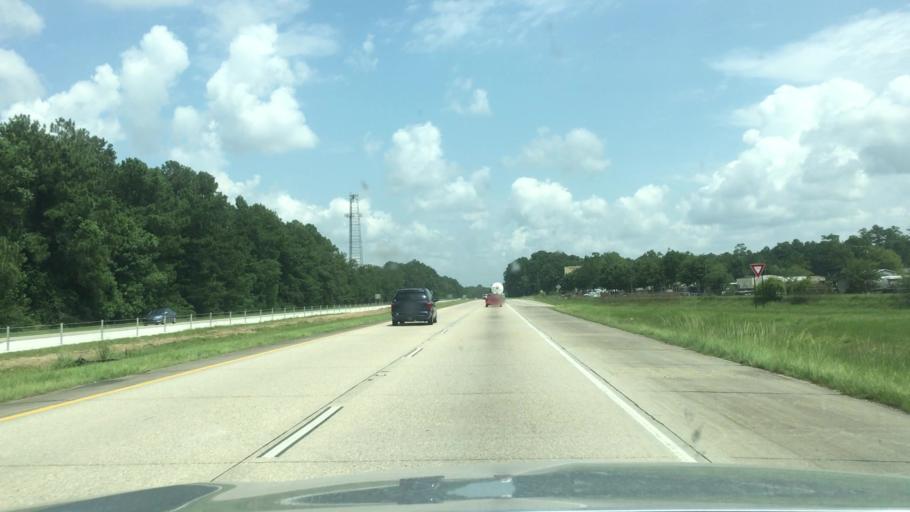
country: US
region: Louisiana
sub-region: Saint Tammany Parish
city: Pearl River
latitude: 30.3539
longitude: -89.7406
